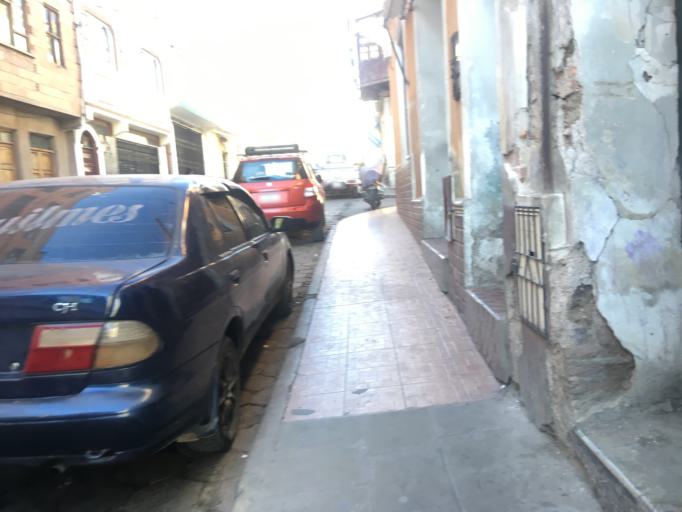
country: BO
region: Potosi
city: Potosi
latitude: -19.5859
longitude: -65.7551
